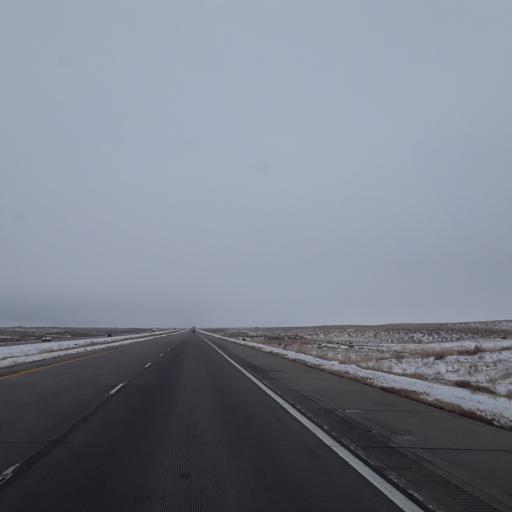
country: US
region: Colorado
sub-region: Logan County
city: Sterling
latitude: 40.5460
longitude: -103.2206
